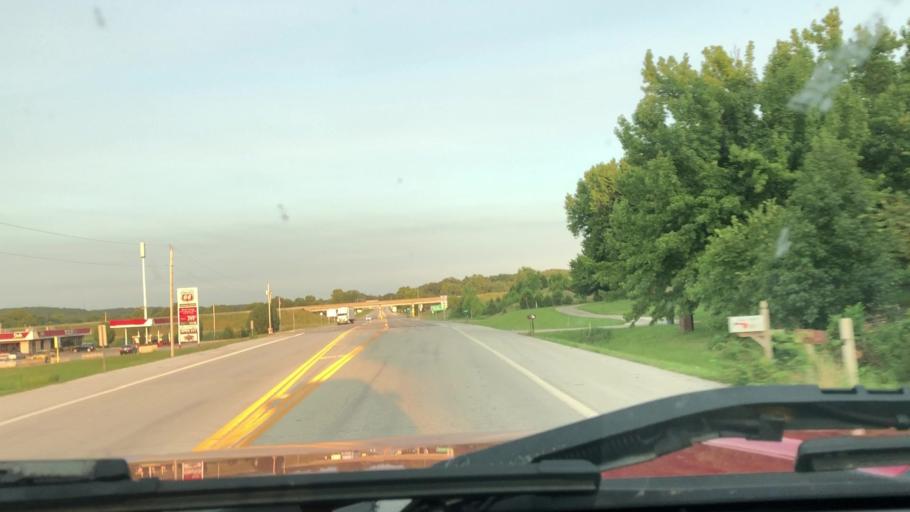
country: US
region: Missouri
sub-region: Jasper County
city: Duquesne
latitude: 36.9689
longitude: -94.4338
